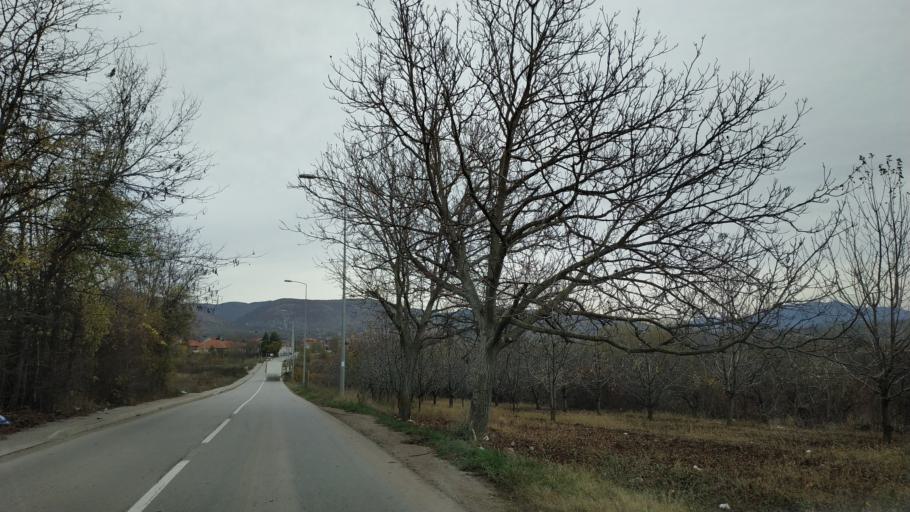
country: RS
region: Central Serbia
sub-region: Nisavski Okrug
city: Nis
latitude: 43.3506
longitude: 21.9403
